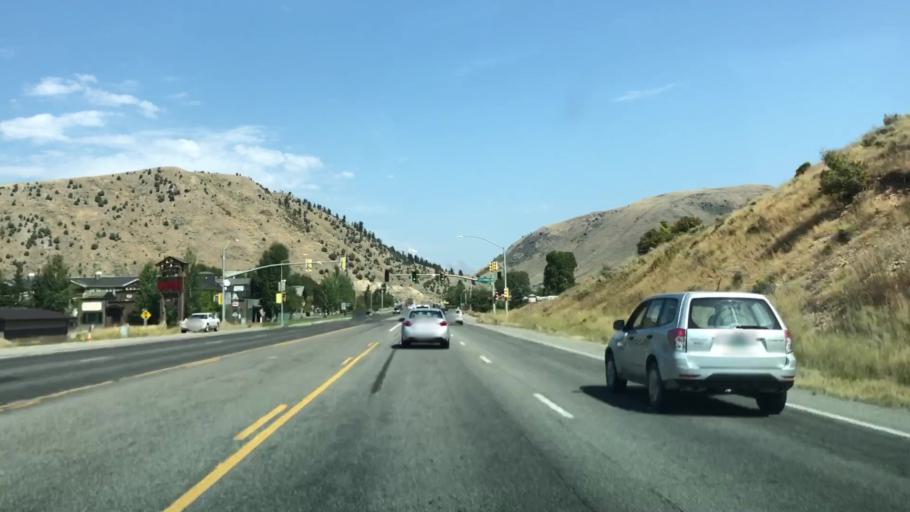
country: US
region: Wyoming
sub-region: Teton County
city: Rafter J Ranch
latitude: 43.4574
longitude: -110.7933
